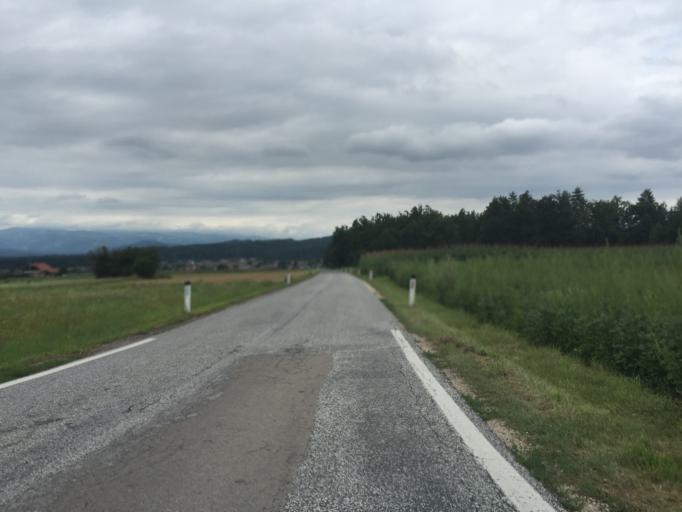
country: AT
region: Carinthia
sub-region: Politischer Bezirk Volkermarkt
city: Feistritz ob Bleiburg
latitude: 46.5601
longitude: 14.7672
